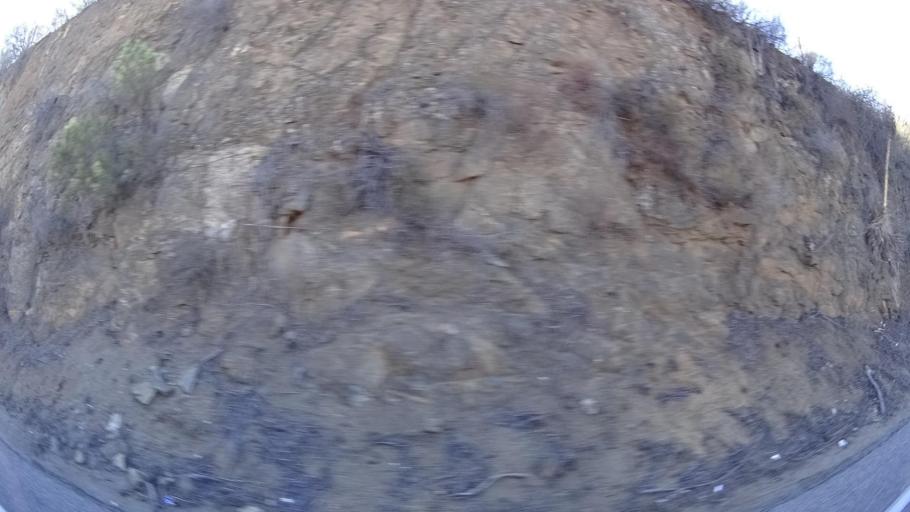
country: US
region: California
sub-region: San Diego County
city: Jamul
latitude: 32.6725
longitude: -116.7796
